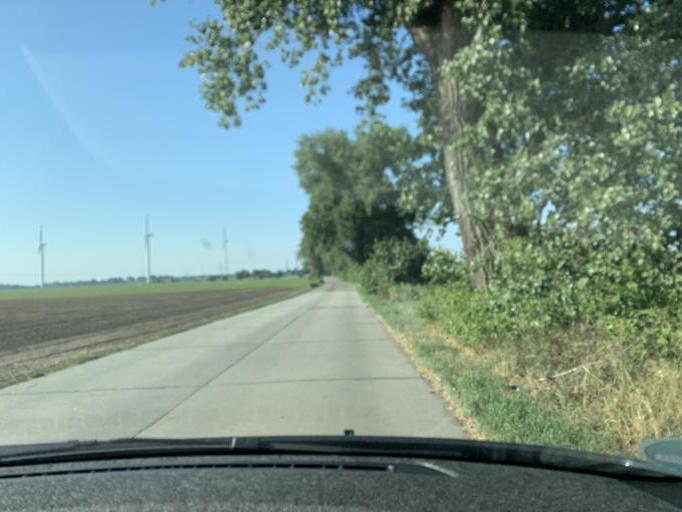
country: DE
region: Brandenburg
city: Zehdenick
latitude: 53.0061
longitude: 13.2737
